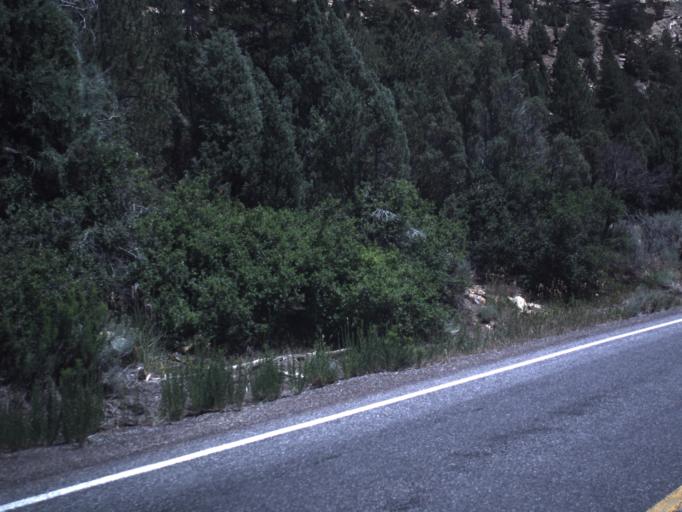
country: US
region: Utah
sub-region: Emery County
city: Huntington
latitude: 39.4142
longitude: -111.1161
